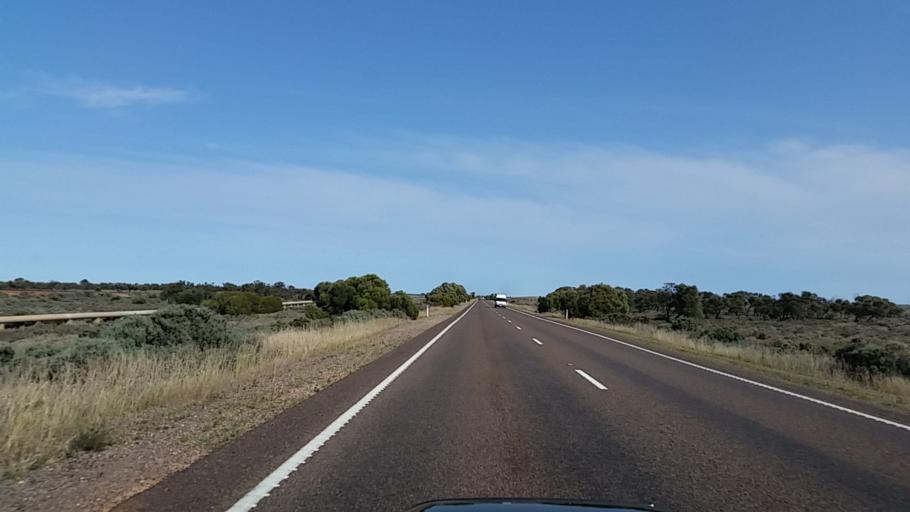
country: AU
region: South Australia
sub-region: Whyalla
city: Whyalla
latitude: -32.8331
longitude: 137.5468
